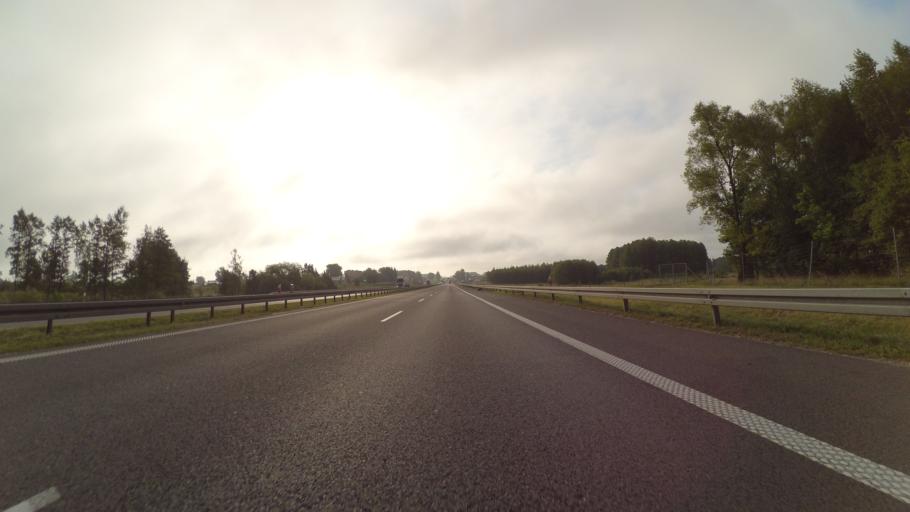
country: PL
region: Podlasie
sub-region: Powiat bialostocki
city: Choroszcz
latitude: 53.1549
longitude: 23.0234
